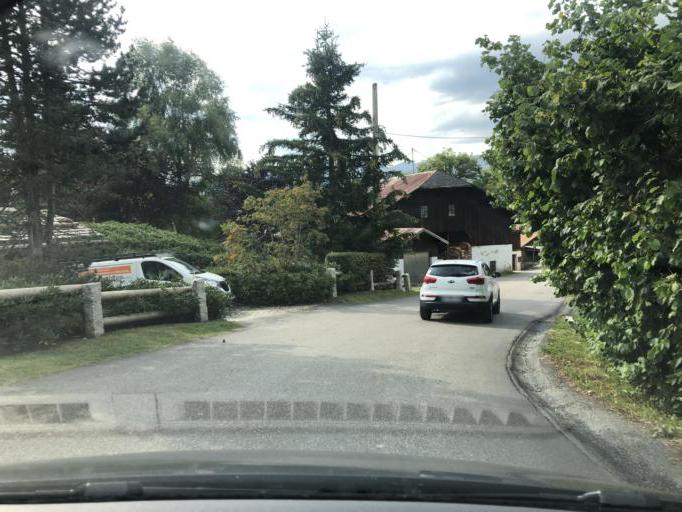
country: FR
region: Rhone-Alpes
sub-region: Departement de la Haute-Savoie
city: Megeve
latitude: 45.8451
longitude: 6.6401
